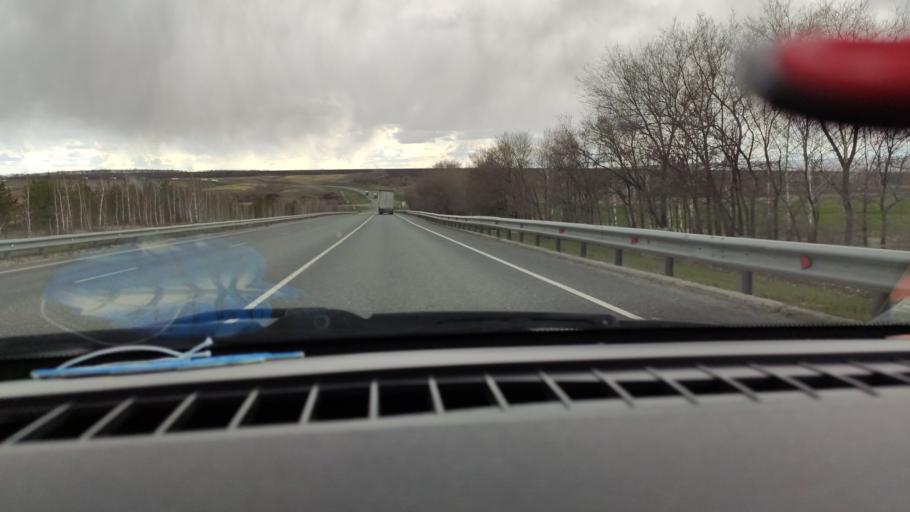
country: RU
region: Saratov
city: Balakovo
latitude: 52.1299
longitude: 47.7617
